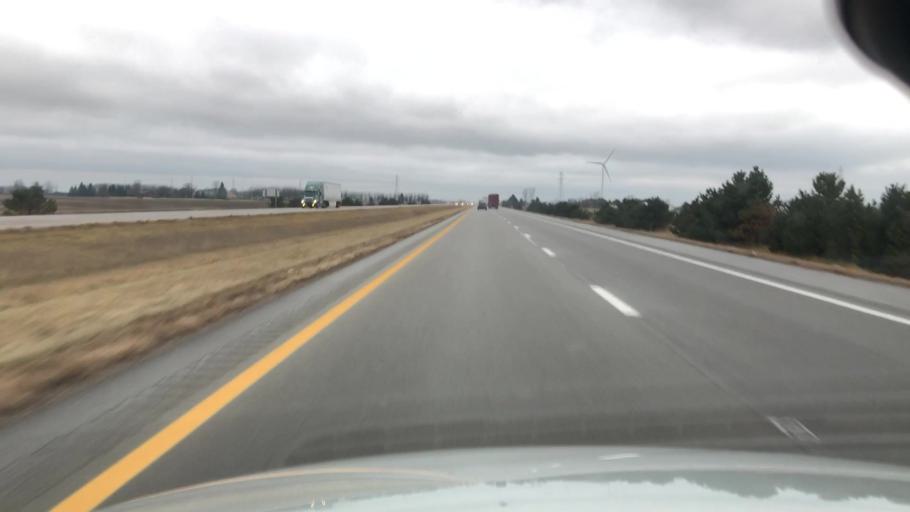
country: US
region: Ohio
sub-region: Van Wert County
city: Convoy
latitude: 40.9195
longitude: -84.6759
